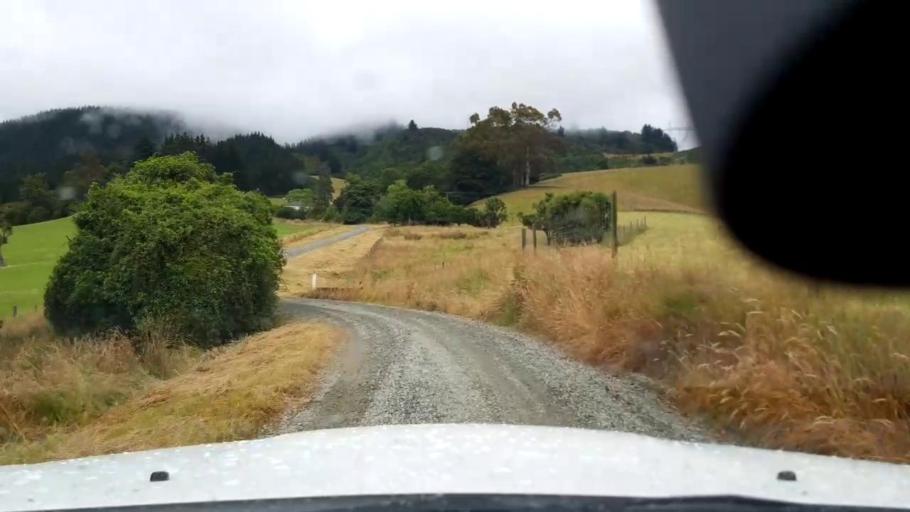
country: NZ
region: Canterbury
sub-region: Timaru District
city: Pleasant Point
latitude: -44.0765
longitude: 171.1423
